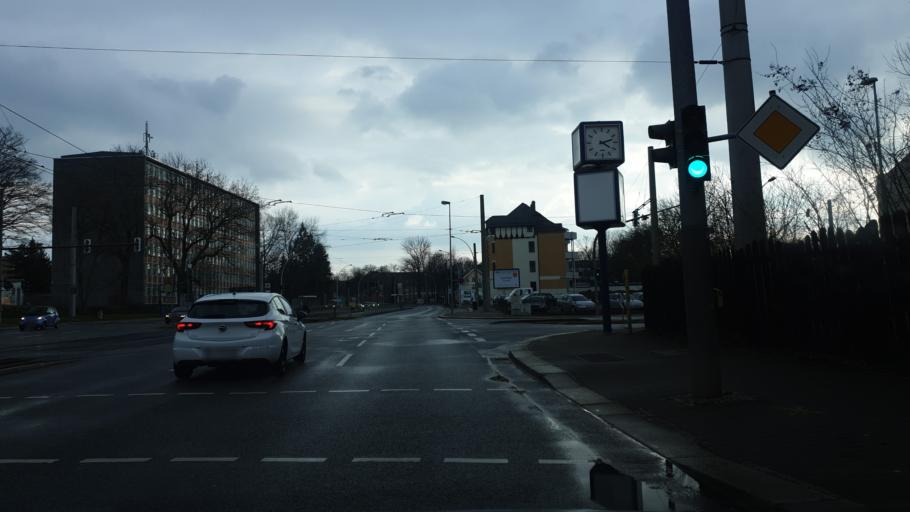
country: DE
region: Saxony
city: Chemnitz
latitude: 50.8031
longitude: 12.9114
